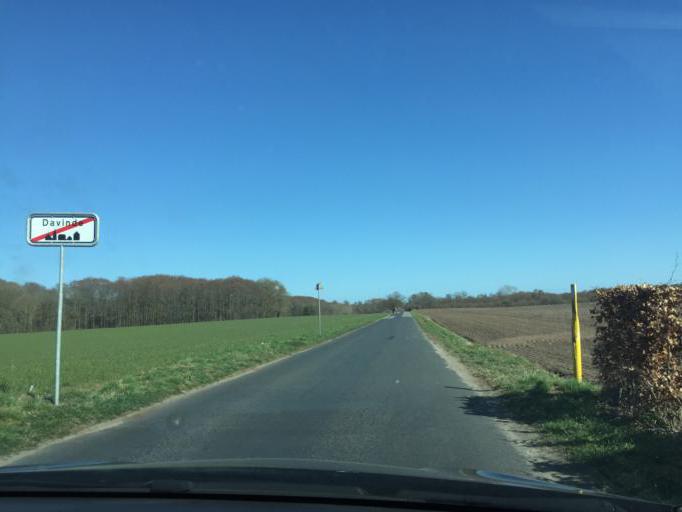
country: DK
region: South Denmark
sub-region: Kerteminde Kommune
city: Langeskov
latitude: 55.3407
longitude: 10.5497
